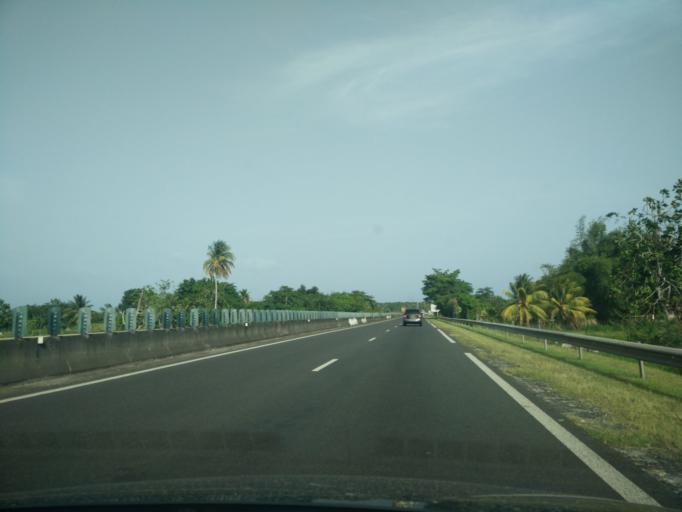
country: GP
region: Guadeloupe
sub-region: Guadeloupe
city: Petit-Bourg
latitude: 16.1760
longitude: -61.5921
